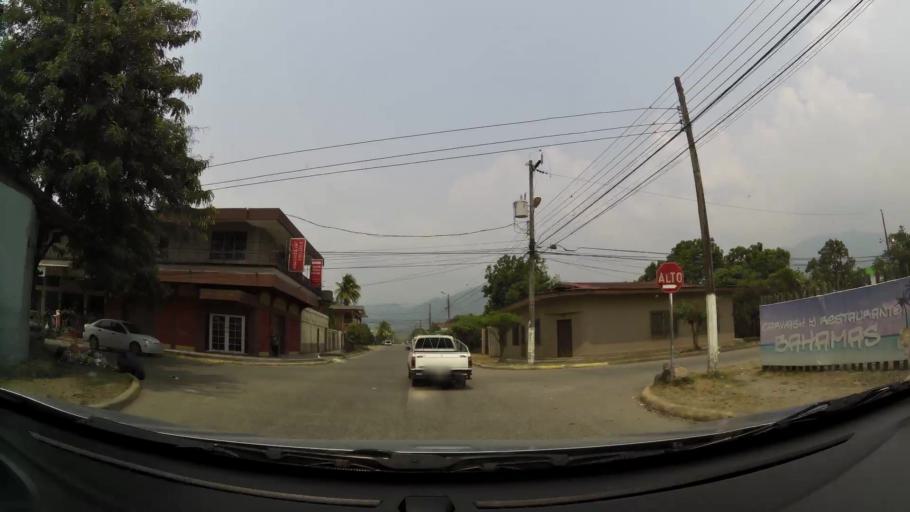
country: HN
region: Yoro
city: El Progreso
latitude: 15.3999
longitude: -87.8058
